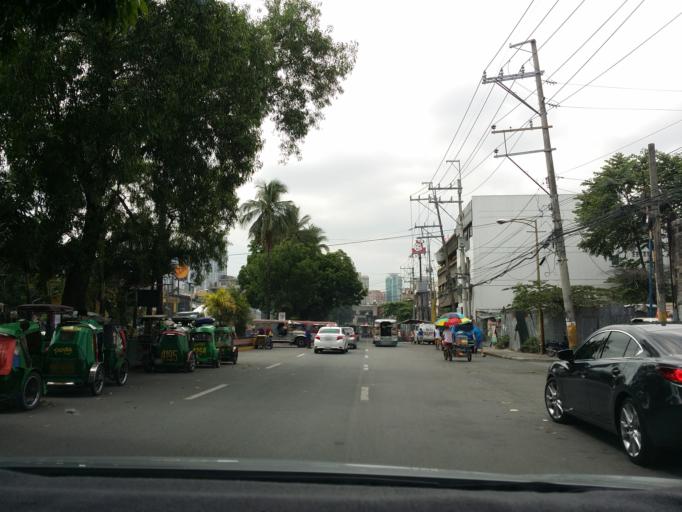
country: PH
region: Metro Manila
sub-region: Mandaluyong
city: Mandaluyong City
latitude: 14.5736
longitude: 121.0161
